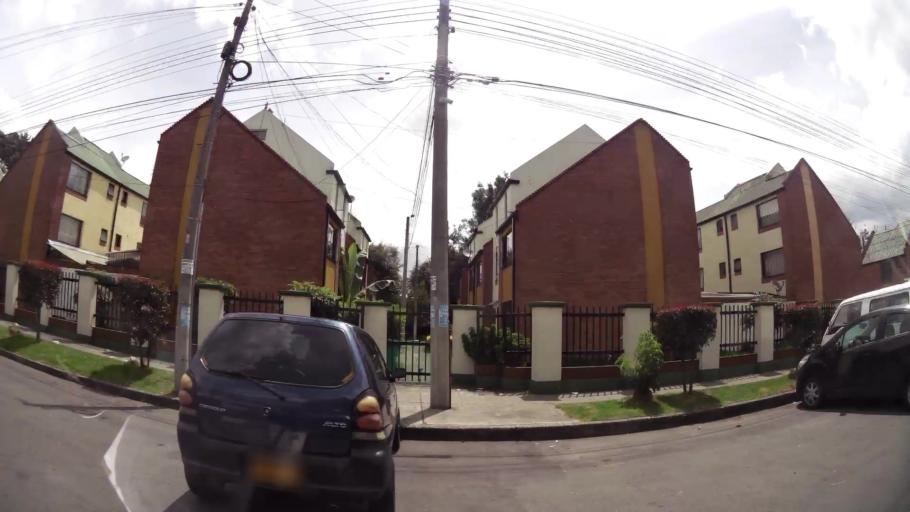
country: CO
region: Bogota D.C.
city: Barrio San Luis
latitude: 4.7084
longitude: -74.1122
